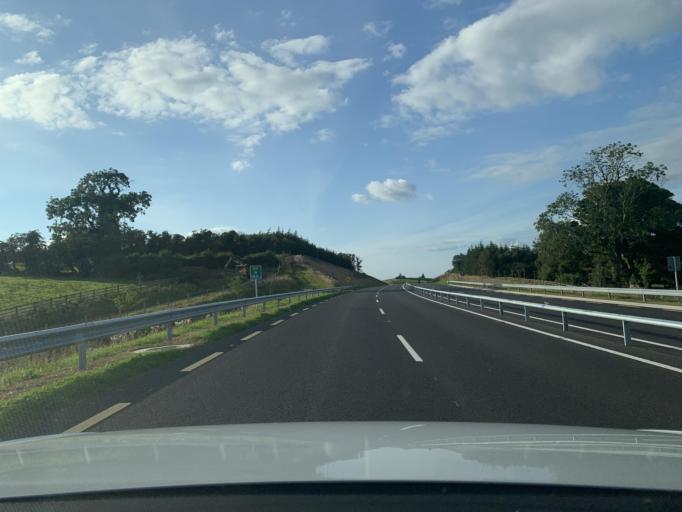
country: IE
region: Connaught
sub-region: Sligo
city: Ballymote
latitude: 54.1041
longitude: -8.4177
